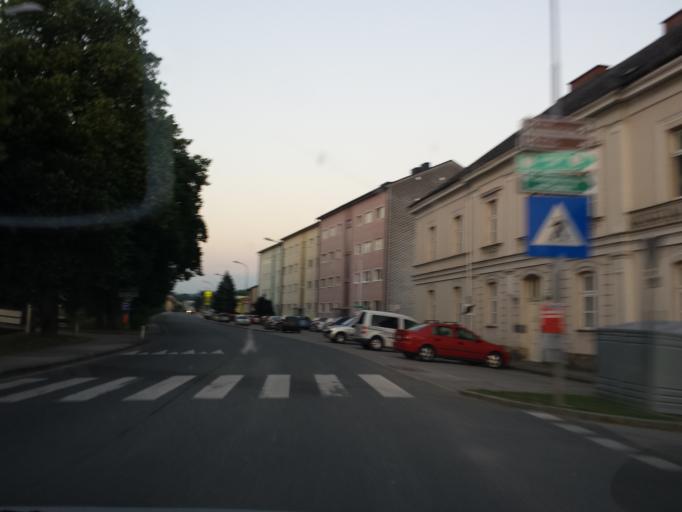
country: AT
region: Lower Austria
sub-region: Politischer Bezirk Lilienfeld
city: Hainfeld
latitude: 48.0341
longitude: 15.7760
